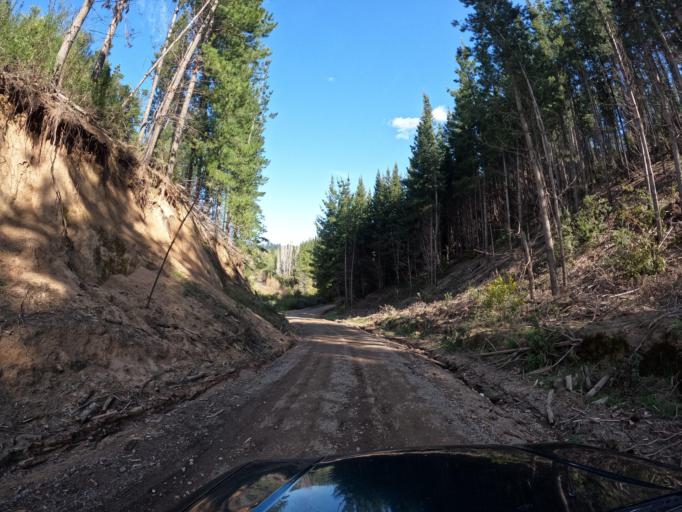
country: CL
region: Biobio
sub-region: Provincia de Concepcion
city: Chiguayante
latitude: -37.0752
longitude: -72.8374
